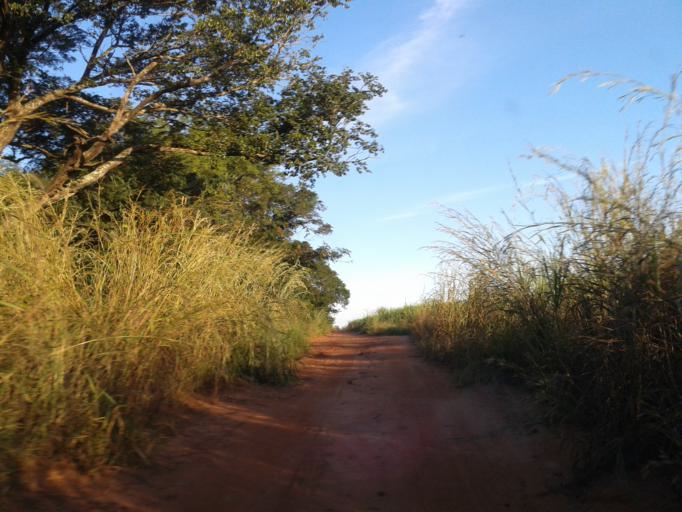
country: BR
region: Minas Gerais
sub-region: Santa Vitoria
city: Santa Vitoria
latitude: -19.0078
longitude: -50.3780
